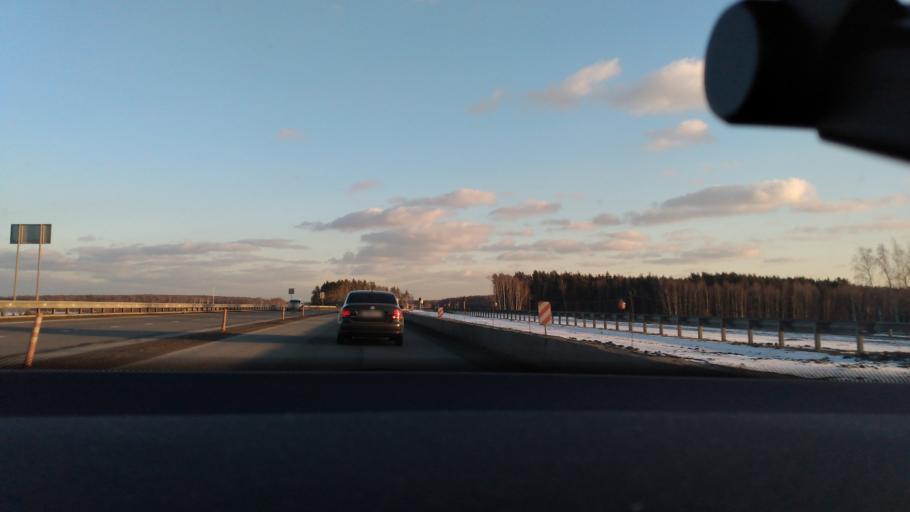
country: RU
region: Moskovskaya
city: Bronnitsy
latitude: 55.3789
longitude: 38.3273
